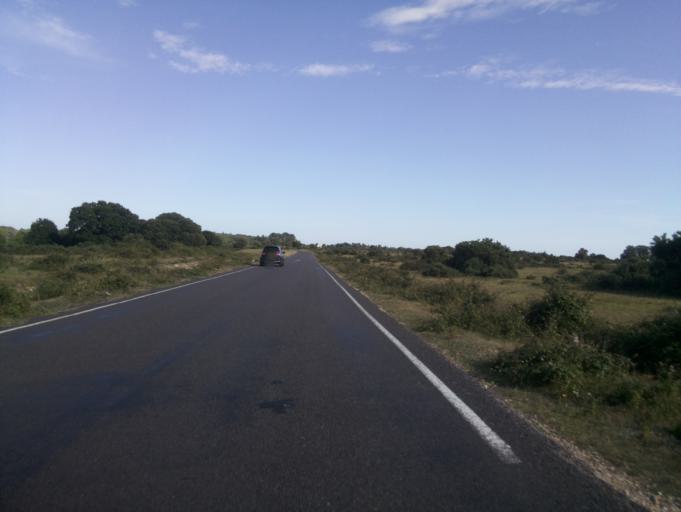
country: GB
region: England
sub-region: Hampshire
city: Cadnam
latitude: 50.9088
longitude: -1.6448
